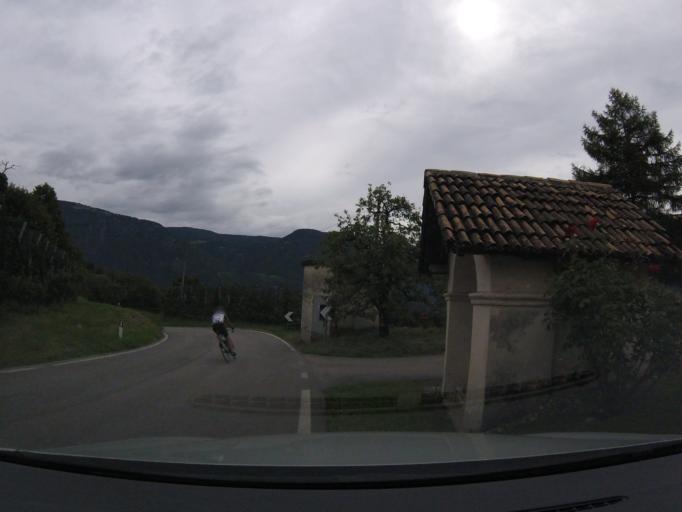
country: IT
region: Trentino-Alto Adige
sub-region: Bolzano
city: Nalles
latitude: 46.5478
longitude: 11.1914
